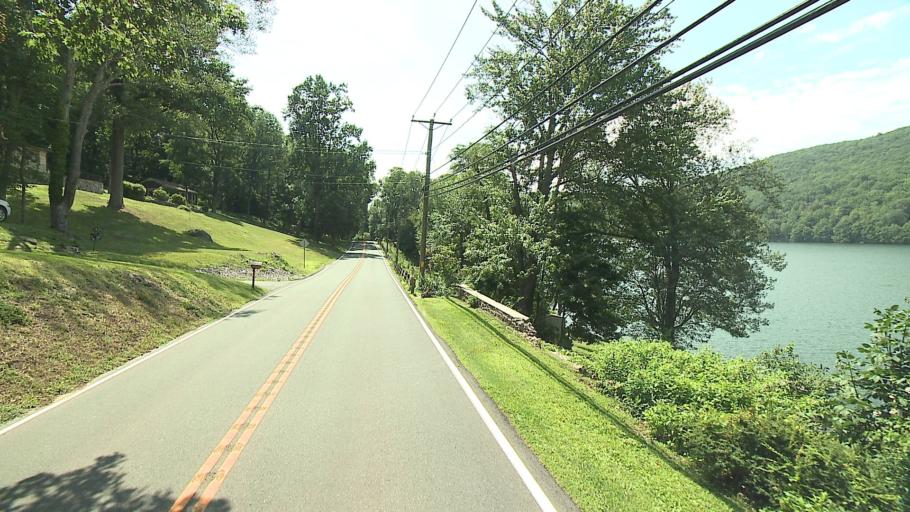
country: US
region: Connecticut
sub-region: Fairfield County
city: Sherman
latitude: 41.5199
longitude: -73.4783
